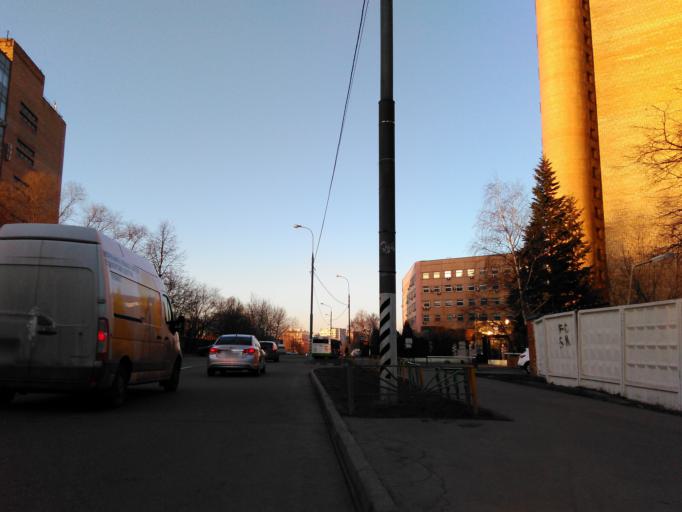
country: RU
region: Moskovskaya
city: Cheremushki
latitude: 55.6461
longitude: 37.5447
